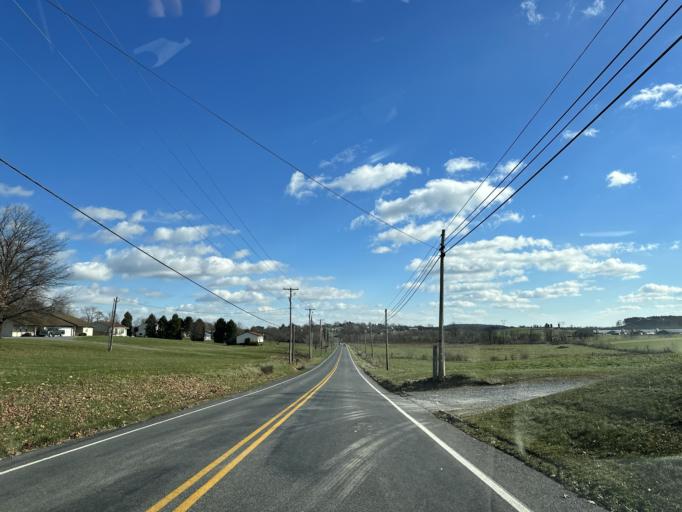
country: US
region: Pennsylvania
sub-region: Lebanon County
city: Myerstown
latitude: 40.4596
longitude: -76.2596
